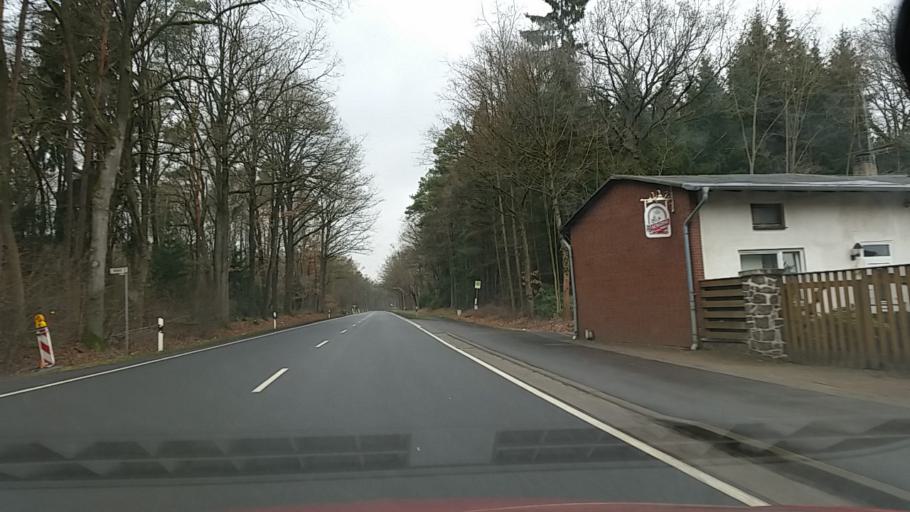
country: DE
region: Lower Saxony
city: Munster
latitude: 53.0100
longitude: 10.0285
